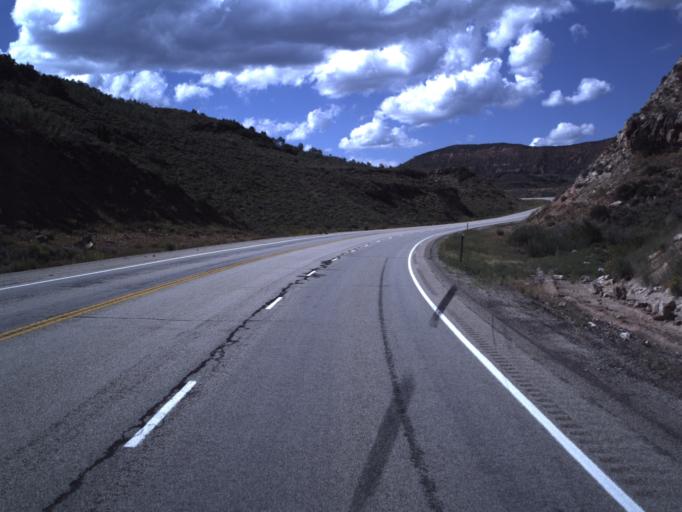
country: US
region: Utah
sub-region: Summit County
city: Francis
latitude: 40.1967
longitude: -110.9668
